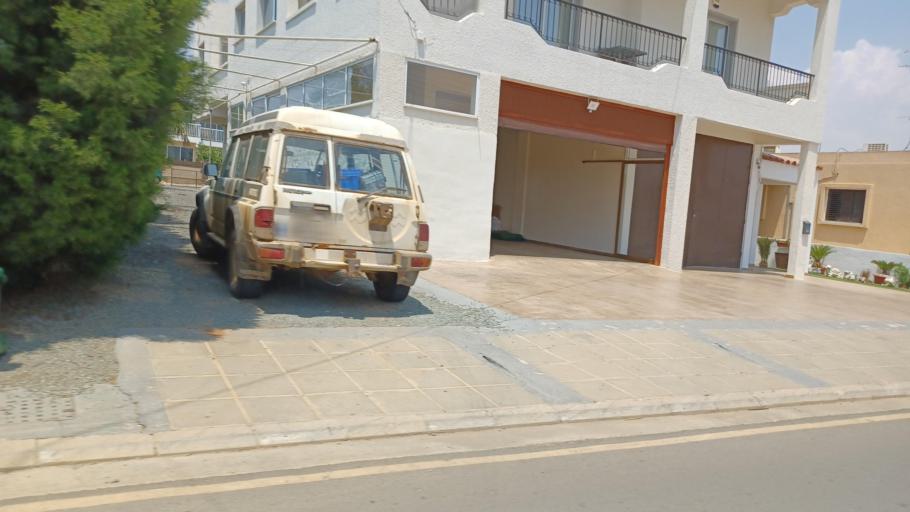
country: CY
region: Ammochostos
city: Liopetri
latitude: 34.9818
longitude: 33.8491
